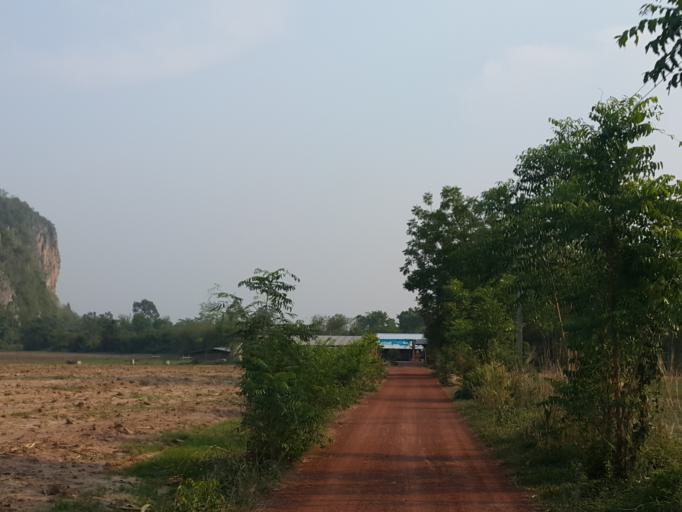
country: TH
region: Uthai Thani
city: Huai Khot
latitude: 15.3208
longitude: 99.6765
